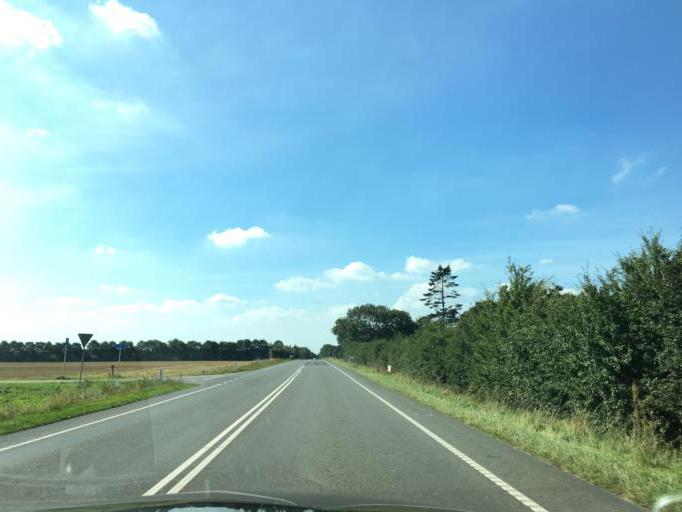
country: DK
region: South Denmark
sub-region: Vejen Kommune
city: Vejen
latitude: 55.4724
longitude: 9.2008
